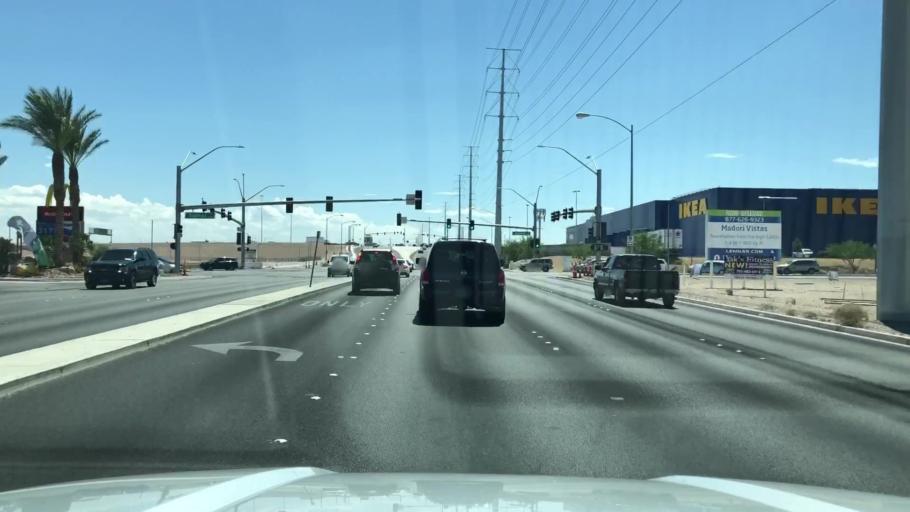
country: US
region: Nevada
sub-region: Clark County
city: Spring Valley
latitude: 36.0711
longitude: -115.2795
